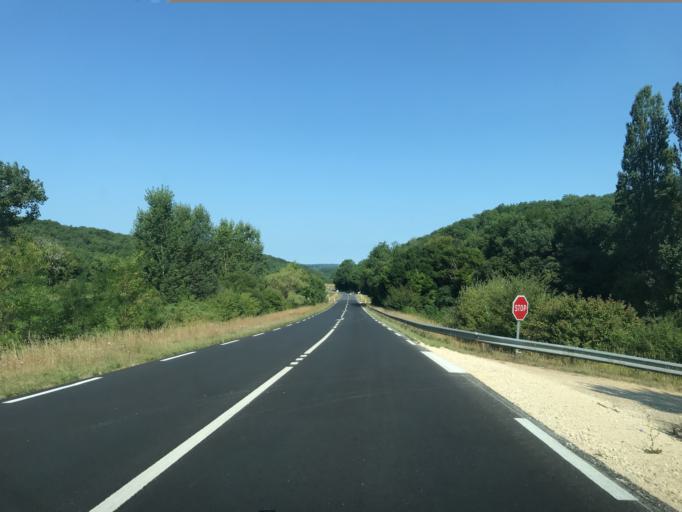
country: FR
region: Aquitaine
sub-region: Departement de la Dordogne
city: Montignac
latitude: 45.0515
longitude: 1.2116
